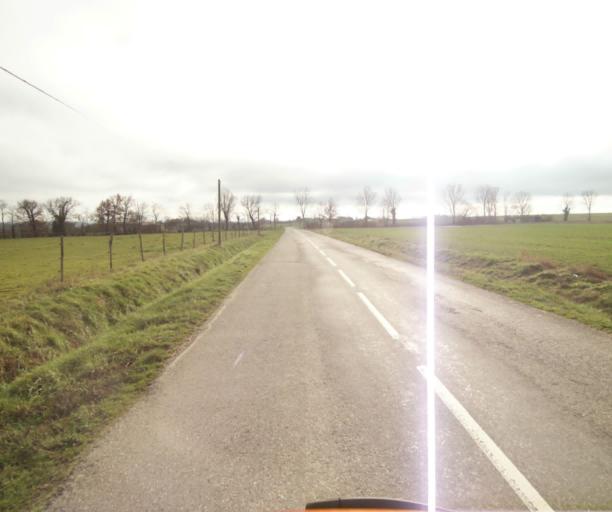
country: FR
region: Languedoc-Roussillon
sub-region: Departement de l'Aude
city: Belpech
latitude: 43.1943
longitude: 1.7295
